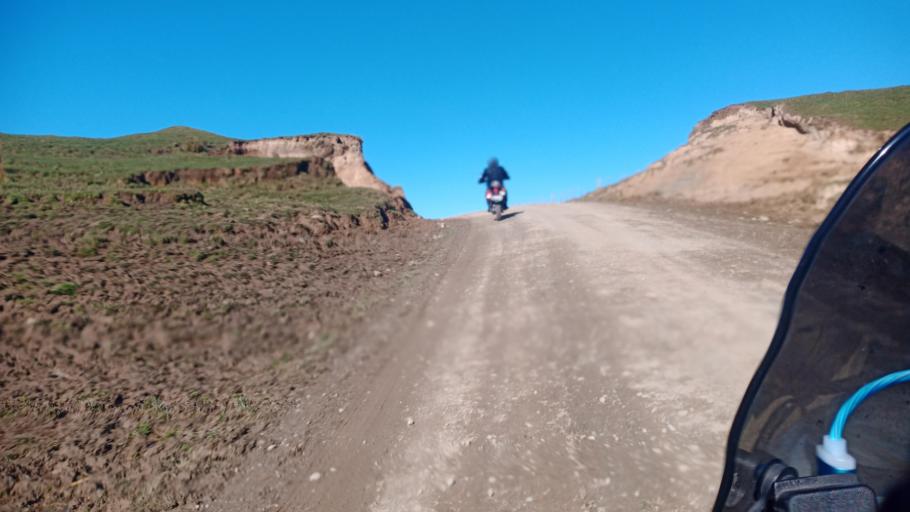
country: NZ
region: Gisborne
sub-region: Gisborne District
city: Gisborne
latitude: -38.2881
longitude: 177.8647
